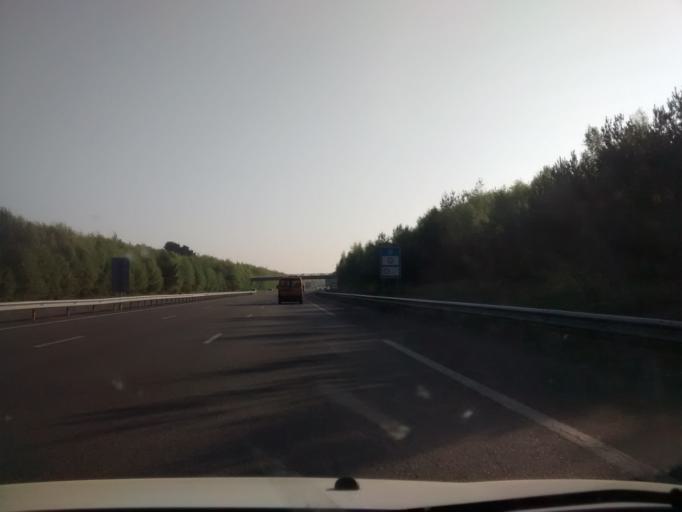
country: FR
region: Brittany
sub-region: Departement d'Ille-et-Vilaine
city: Fouillard
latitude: 48.1617
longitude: -1.5927
